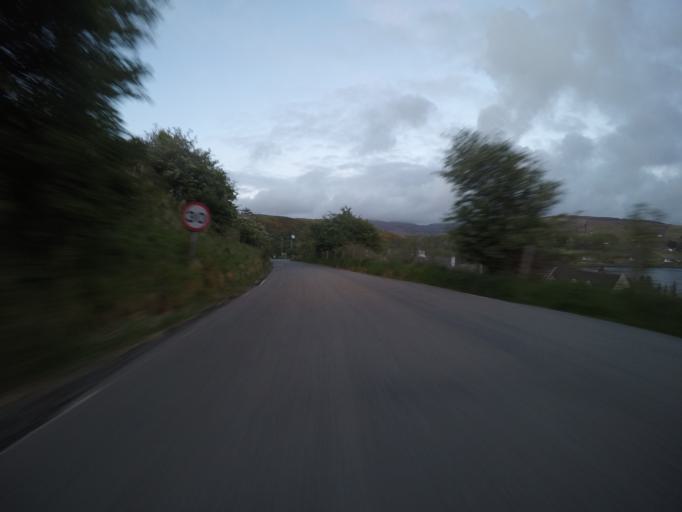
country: GB
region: Scotland
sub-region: Highland
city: Portree
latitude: 57.5918
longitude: -6.3668
